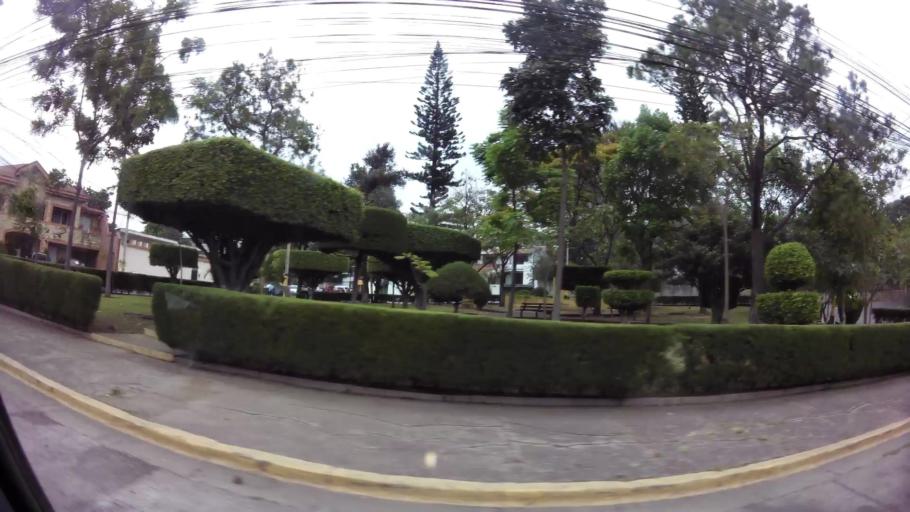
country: HN
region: Francisco Morazan
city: Tegucigalpa
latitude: 14.1022
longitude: -87.1935
